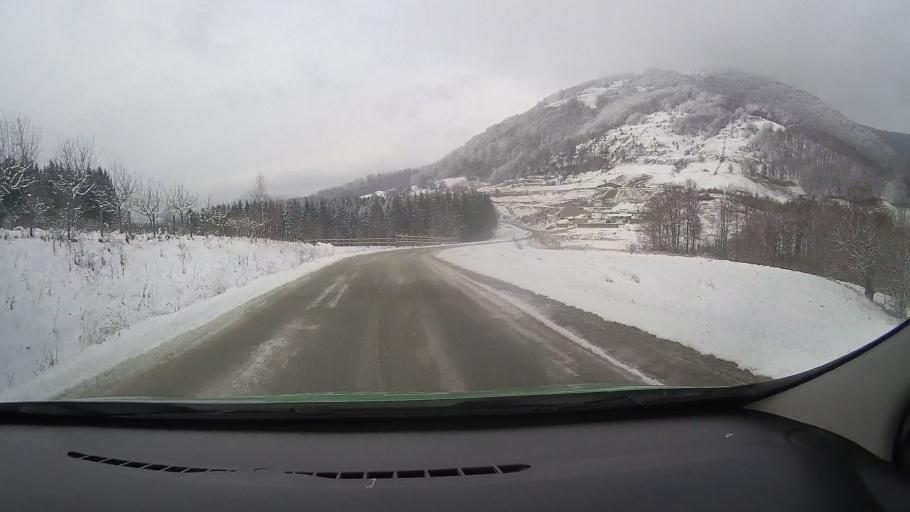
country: RO
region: Alba
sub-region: Comuna Almasu Mare
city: Almasu Mare
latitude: 46.0965
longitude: 23.1594
